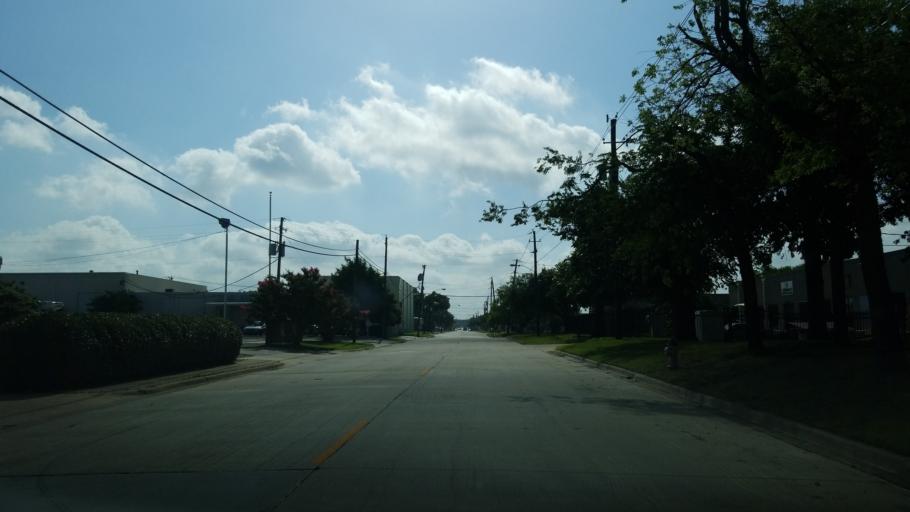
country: US
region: Texas
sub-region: Dallas County
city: Farmers Branch
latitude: 32.8863
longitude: -96.8957
